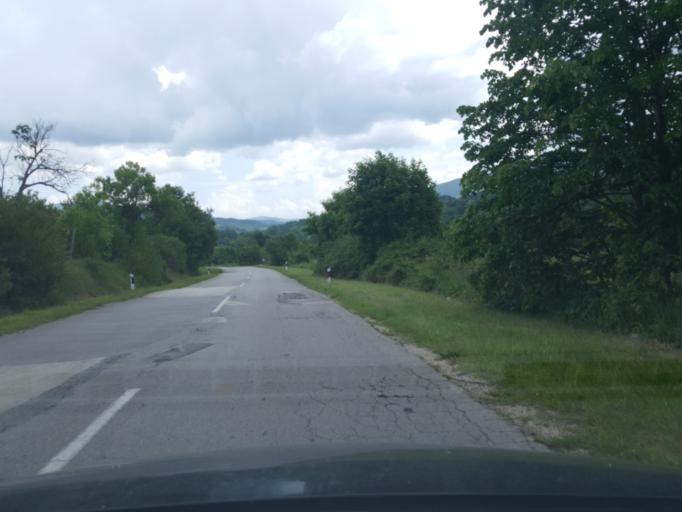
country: RS
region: Central Serbia
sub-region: Zajecarski Okrug
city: Soko Banja
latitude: 43.6455
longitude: 21.9028
